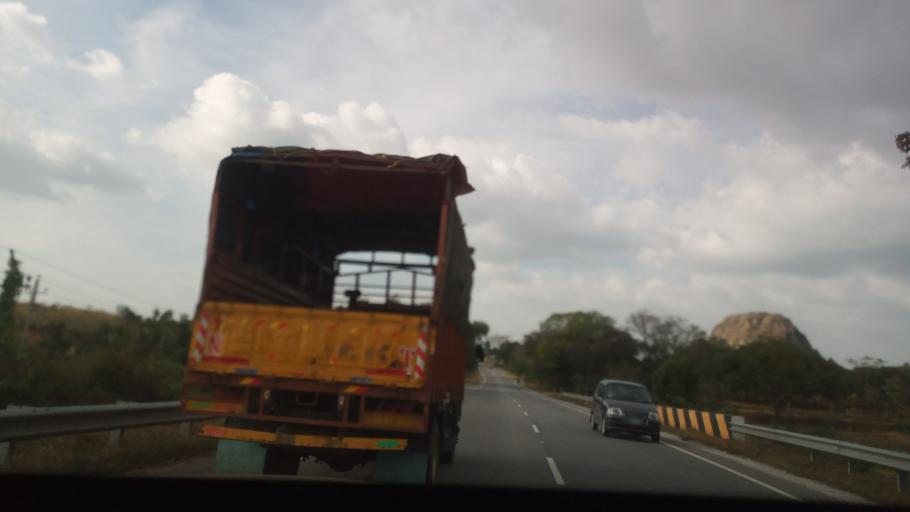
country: IN
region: Karnataka
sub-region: Tumkur
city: Kunigal
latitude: 12.8099
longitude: 77.0367
